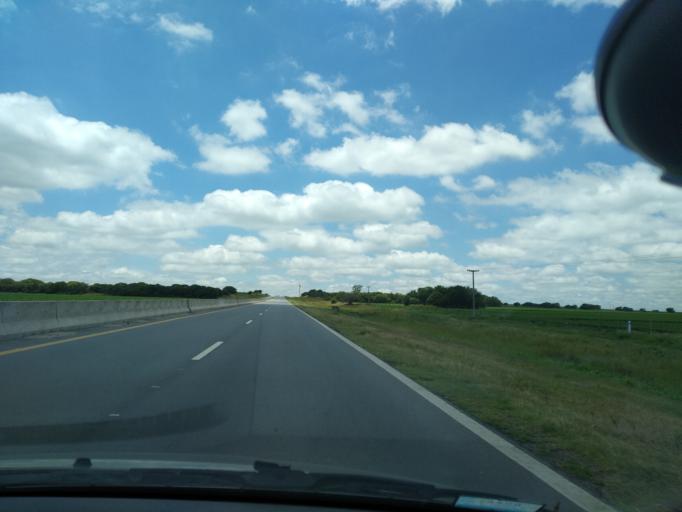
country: AR
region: Cordoba
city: Alta Gracia
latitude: -31.6524
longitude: -64.3367
